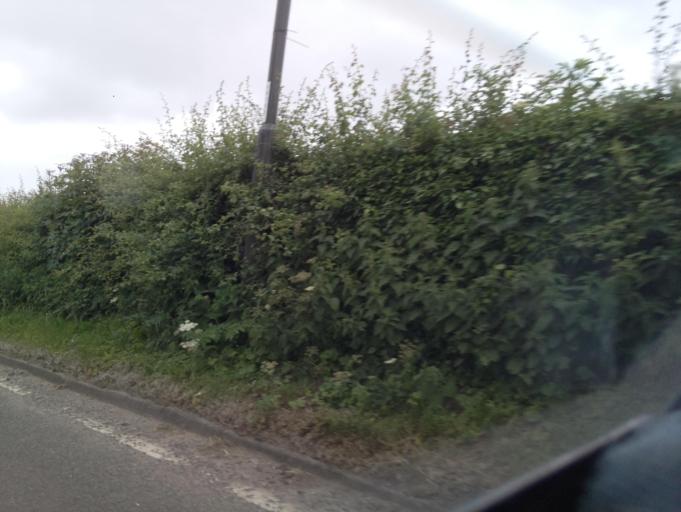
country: GB
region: England
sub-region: Derby
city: Derby
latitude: 52.9338
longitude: -1.5304
